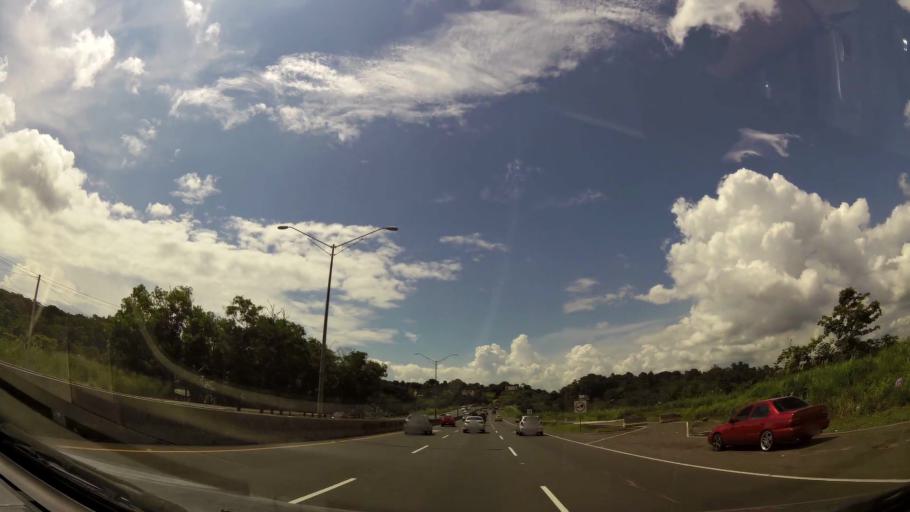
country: PA
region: Panama
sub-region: Distrito Arraijan
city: Arraijan
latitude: 8.9479
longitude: -79.6647
